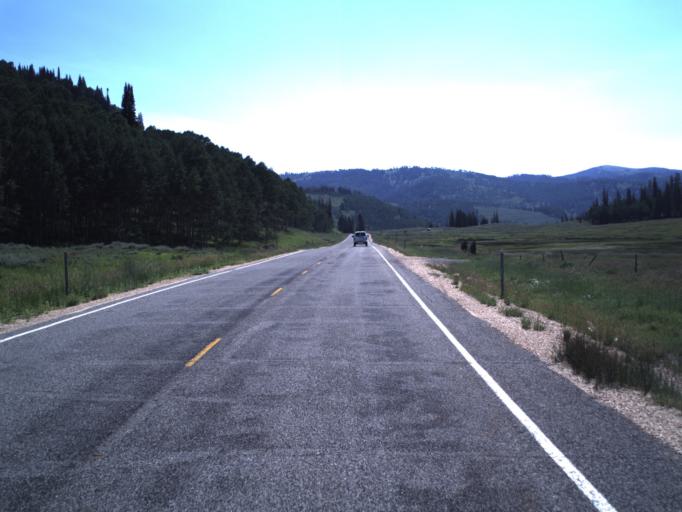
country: US
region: Utah
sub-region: Sanpete County
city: Fairview
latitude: 39.6488
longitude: -111.2679
